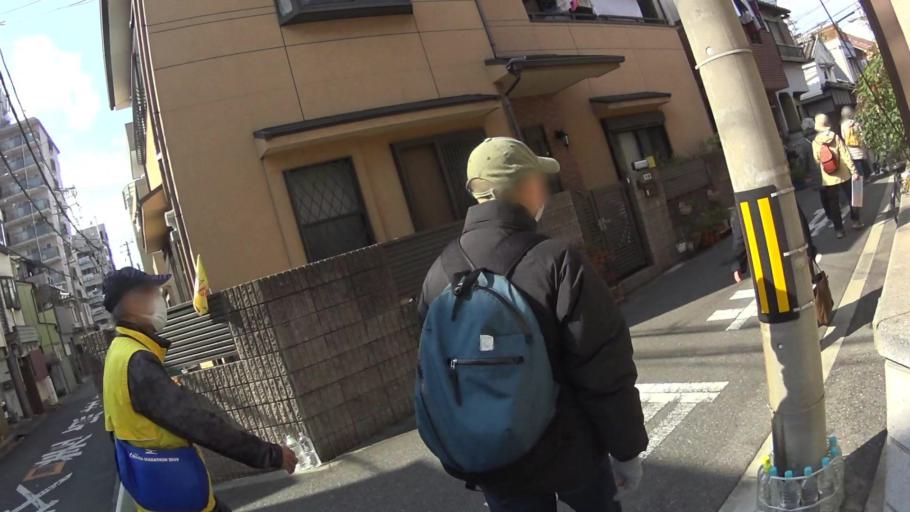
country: JP
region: Osaka
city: Sakai
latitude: 34.6175
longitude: 135.4935
